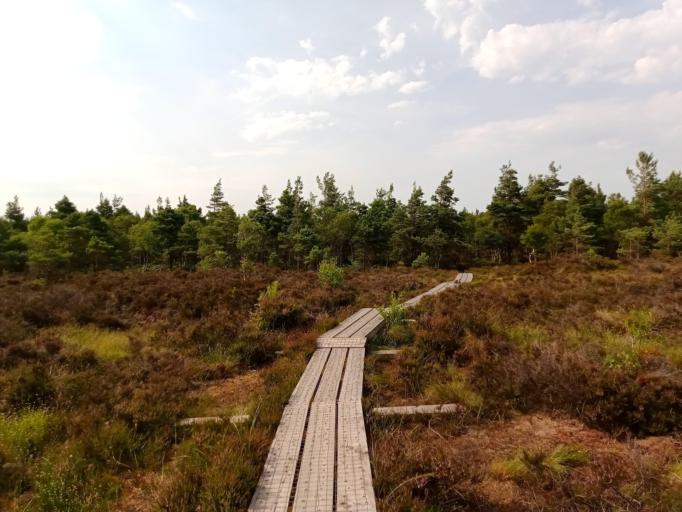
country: IE
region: Leinster
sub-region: Laois
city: Abbeyleix
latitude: 52.8943
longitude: -7.3555
